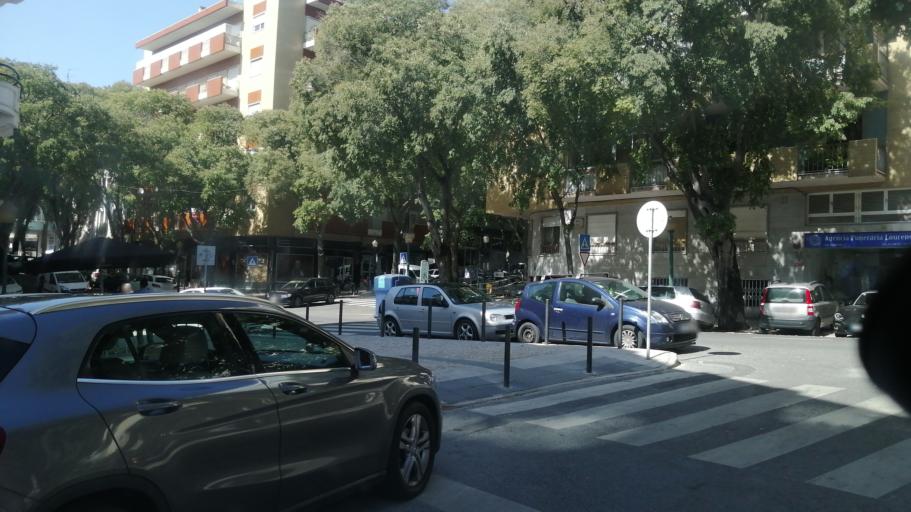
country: PT
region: Setubal
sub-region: Almada
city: Pragal
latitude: 38.7053
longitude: -9.1827
